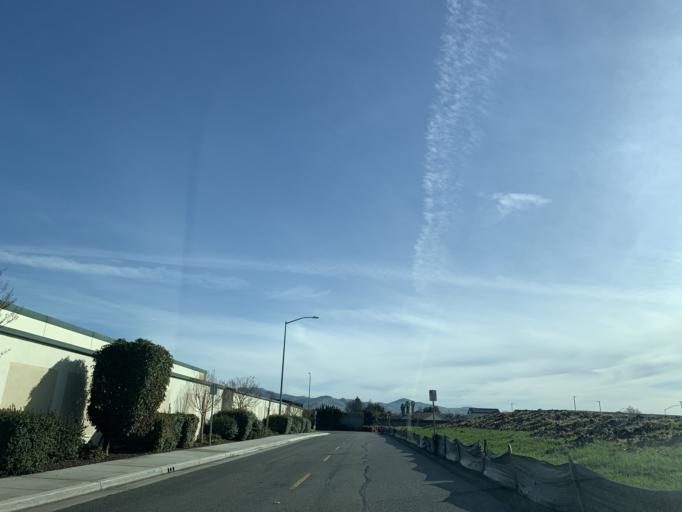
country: US
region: California
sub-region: San Benito County
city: Hollister
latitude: 36.8445
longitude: -121.3929
